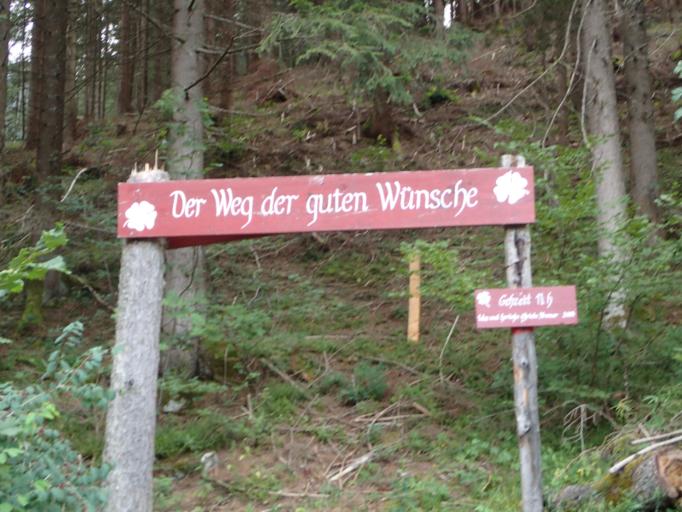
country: AT
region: Salzburg
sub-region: Politischer Bezirk Sankt Johann im Pongau
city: Flachau
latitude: 47.3434
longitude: 13.3970
